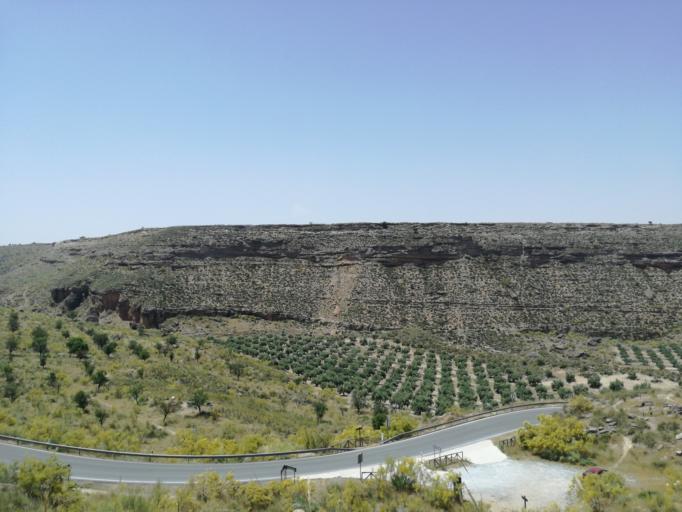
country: ES
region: Andalusia
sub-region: Provincia de Granada
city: Gor
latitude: 37.4490
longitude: -3.0206
